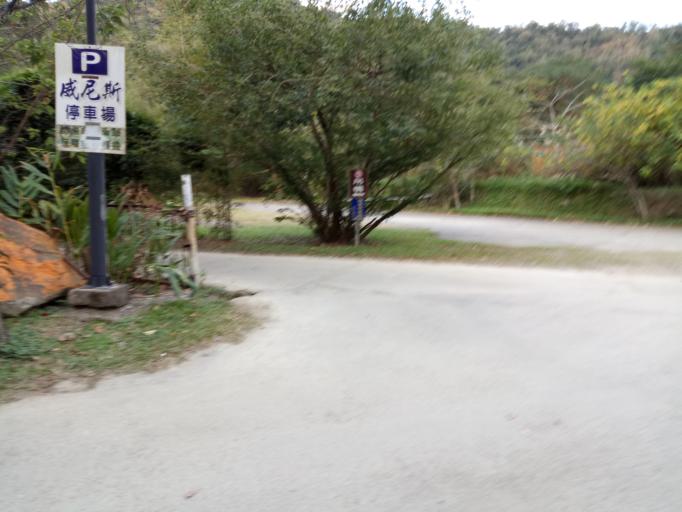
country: TW
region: Taiwan
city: Daxi
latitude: 24.7010
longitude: 121.1830
